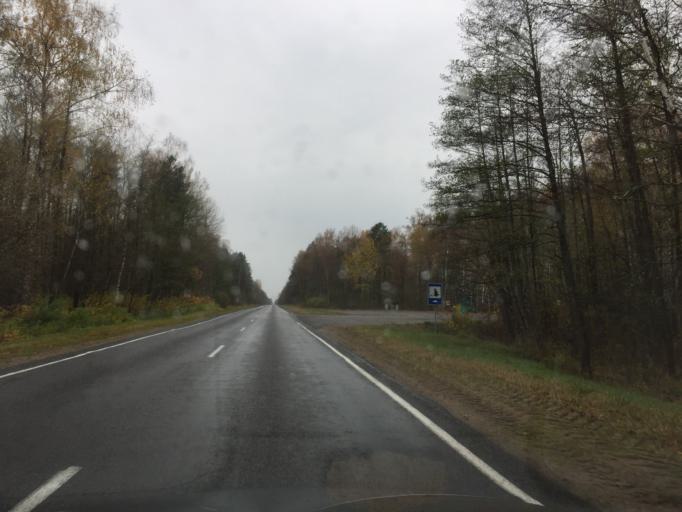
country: BY
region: Mogilev
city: Slawharad
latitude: 53.3608
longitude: 30.8426
